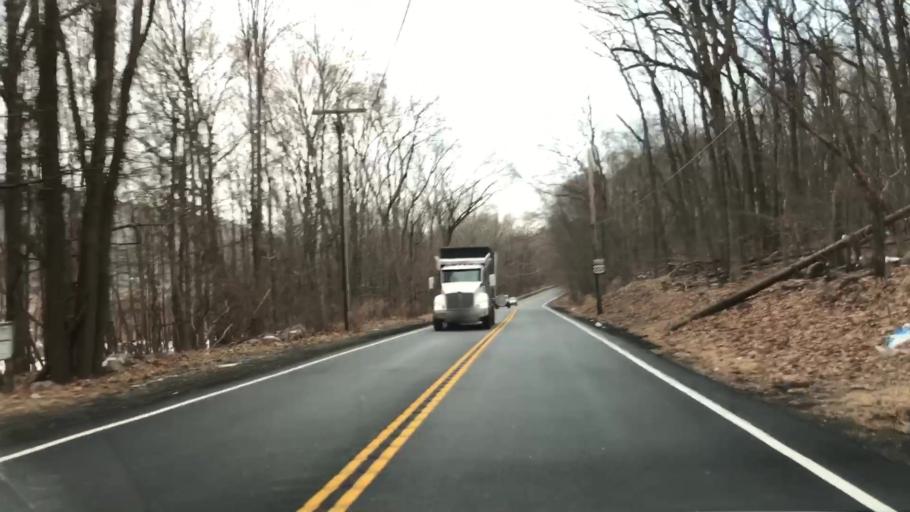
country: US
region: New York
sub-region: Rockland County
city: Wesley Hills
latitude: 41.1765
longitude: -74.0796
